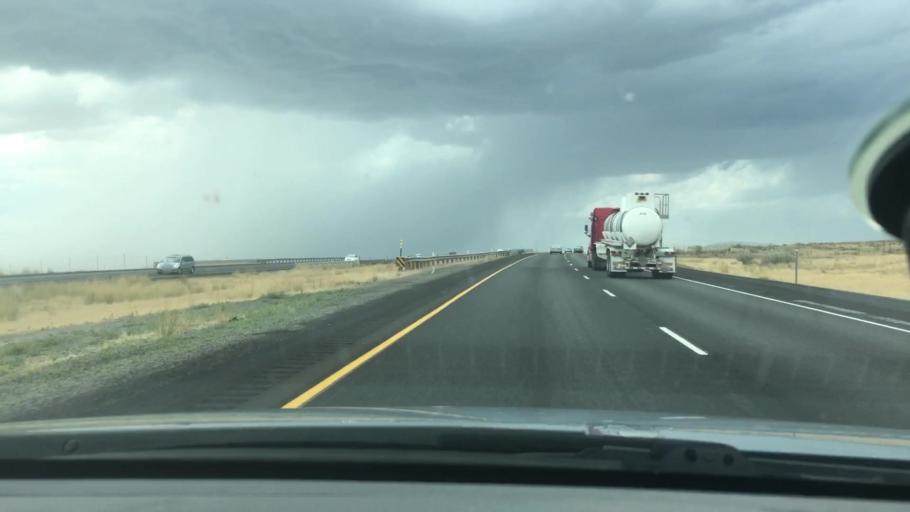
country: US
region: Utah
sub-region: Juab County
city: Mona
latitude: 39.7918
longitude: -111.8383
